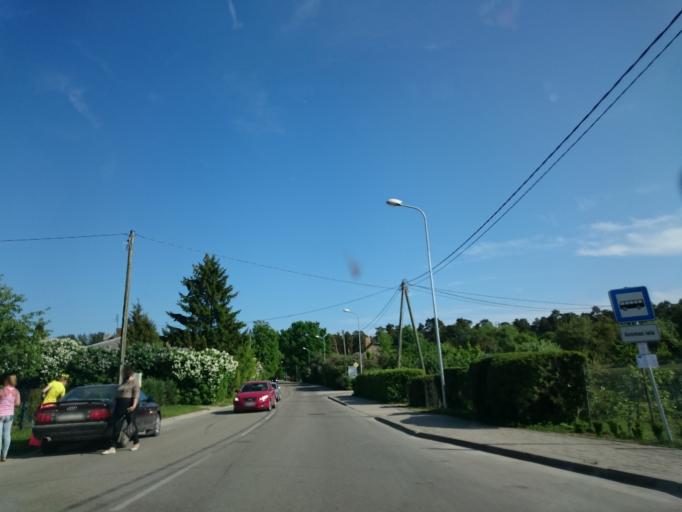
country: LV
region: Dobeles Rajons
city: Dobele
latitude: 56.6105
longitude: 23.2854
